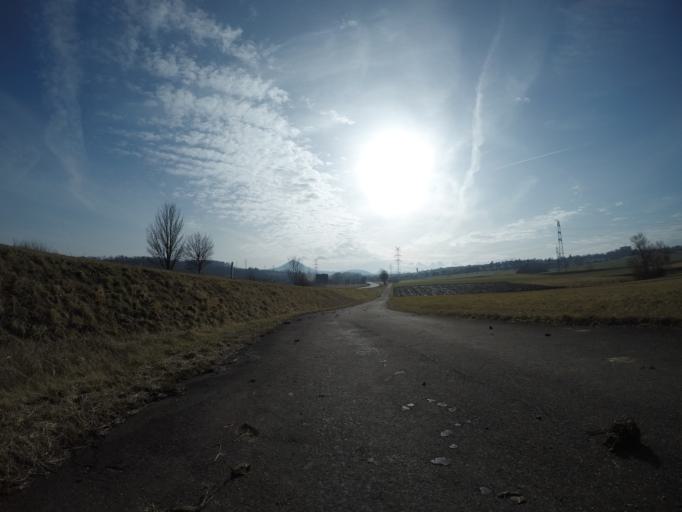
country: DE
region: Baden-Wuerttemberg
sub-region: Tuebingen Region
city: Pliezhausen
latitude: 48.5310
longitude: 9.2277
